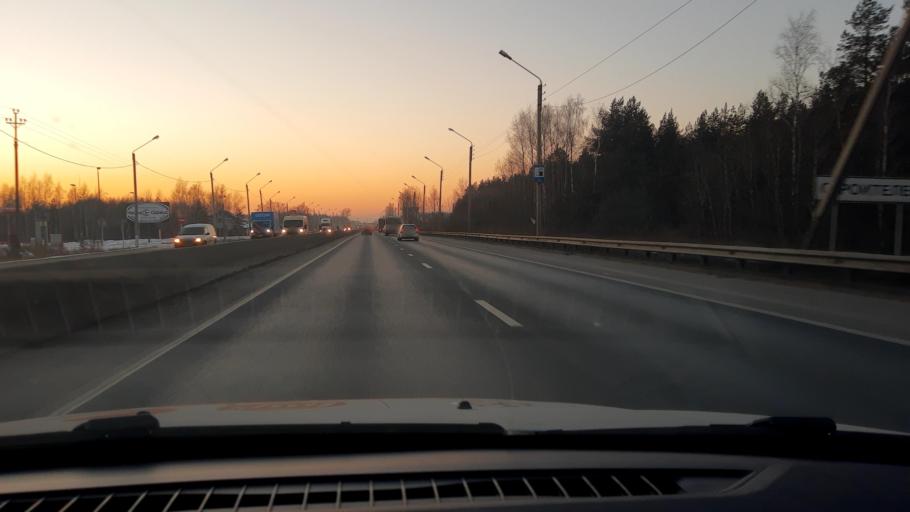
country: RU
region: Nizjnij Novgorod
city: Gorbatovka
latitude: 56.3077
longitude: 43.7050
